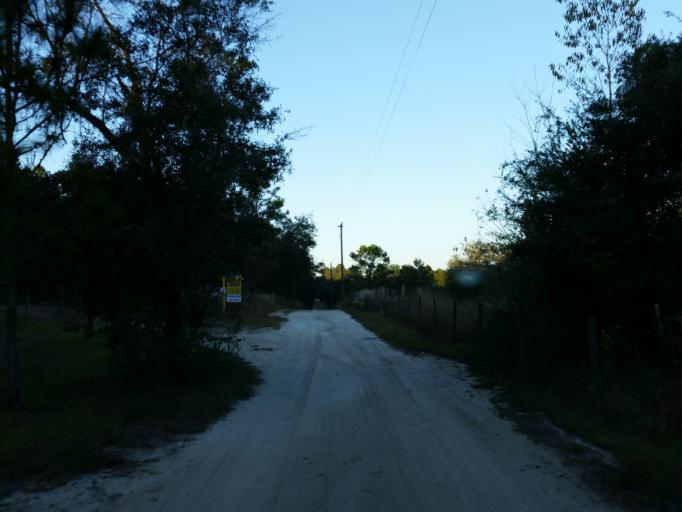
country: US
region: Florida
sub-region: Hernando County
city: Hill 'n Dale
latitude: 28.5293
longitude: -82.2508
